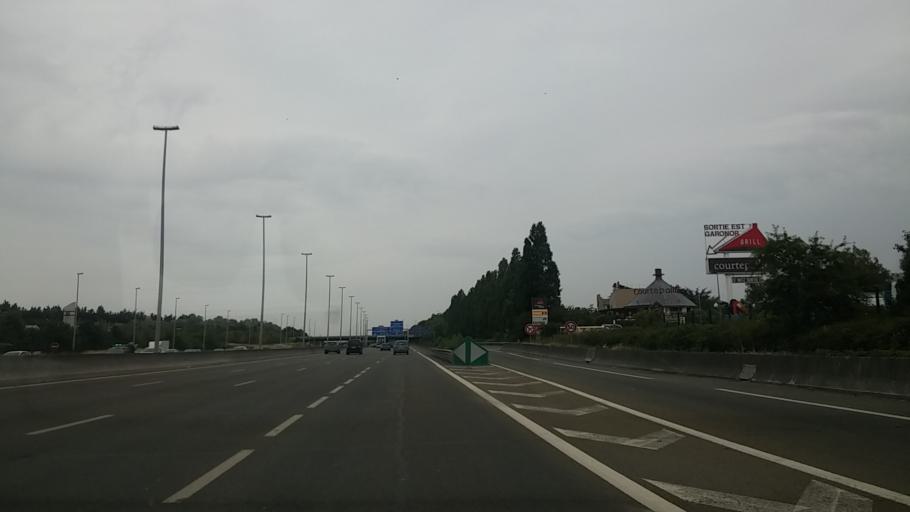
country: FR
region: Ile-de-France
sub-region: Departement de Seine-Saint-Denis
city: Le Blanc-Mesnil
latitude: 48.9581
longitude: 2.4639
